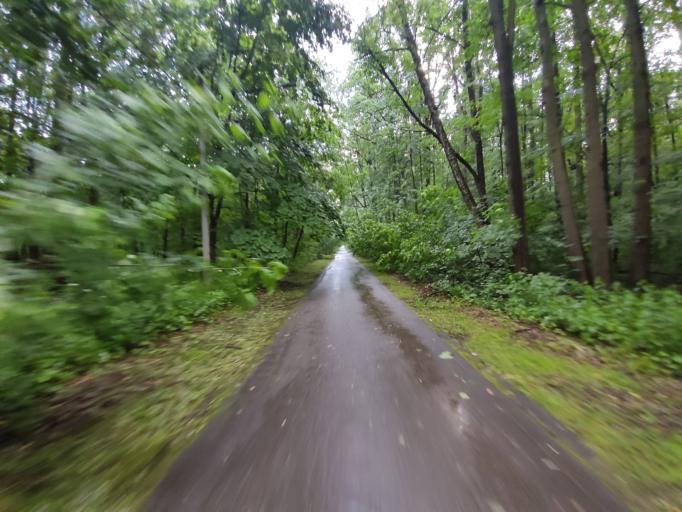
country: RU
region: Moscow
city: Metrogorodok
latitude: 55.7859
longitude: 37.7585
